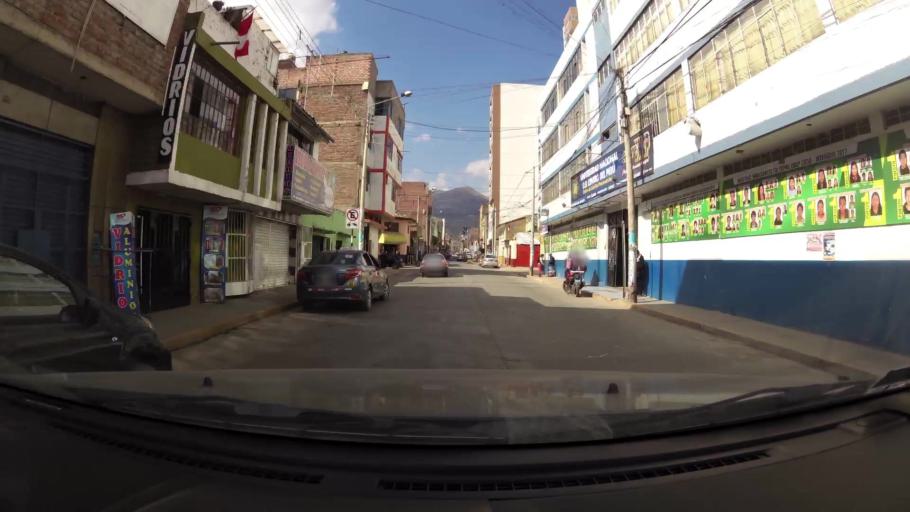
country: PE
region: Junin
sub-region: Provincia de Huancayo
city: El Tambo
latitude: -12.0757
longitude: -75.2098
